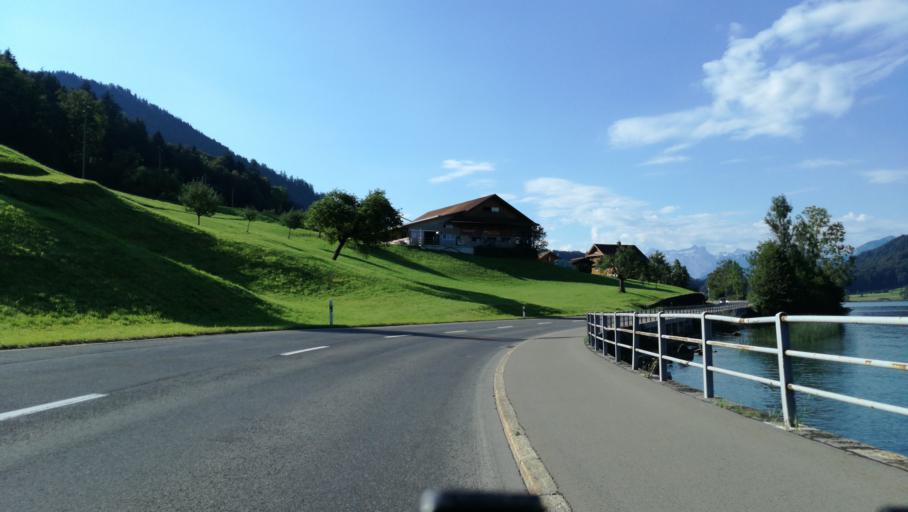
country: CH
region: Schwyz
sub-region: Bezirk Schwyz
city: Sattel
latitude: 47.1140
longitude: 8.6433
